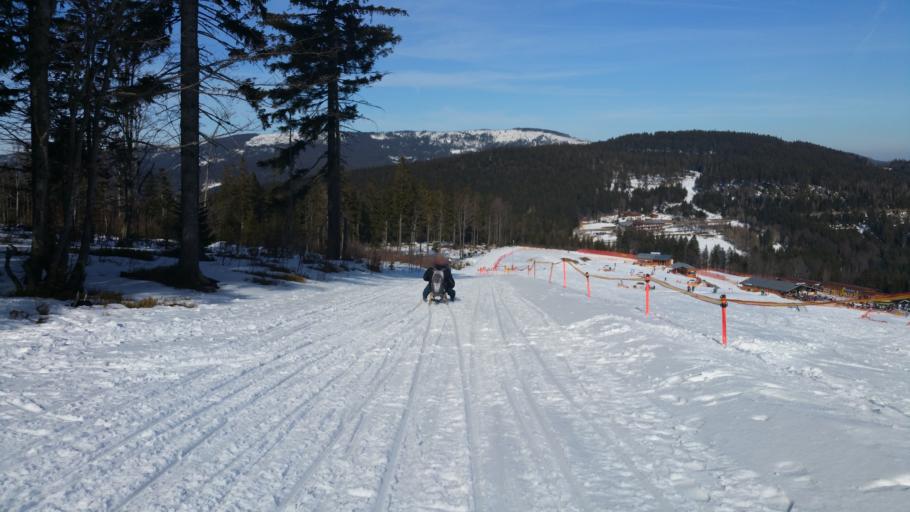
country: DE
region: Bavaria
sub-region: Upper Palatinate
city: Lohberg
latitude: 49.1287
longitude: 13.1367
